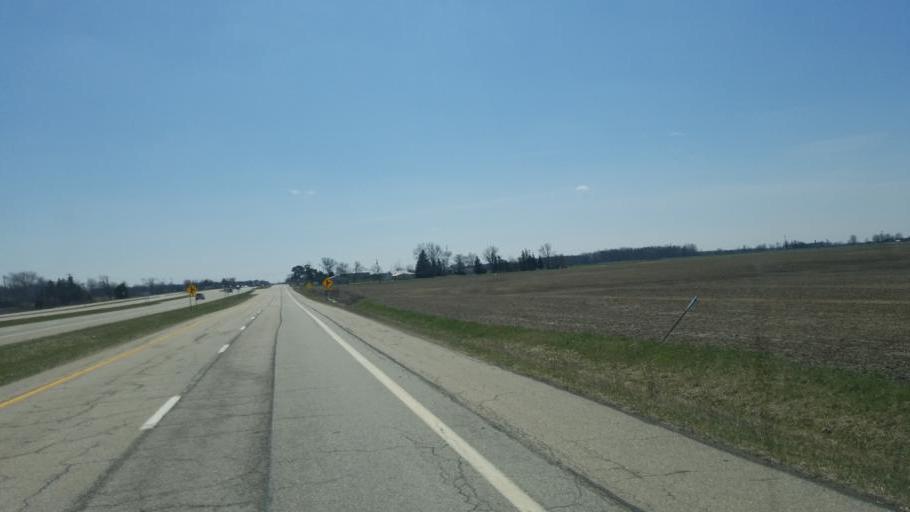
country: US
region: Ohio
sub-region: Delaware County
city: Delaware
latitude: 40.3985
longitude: -83.0744
